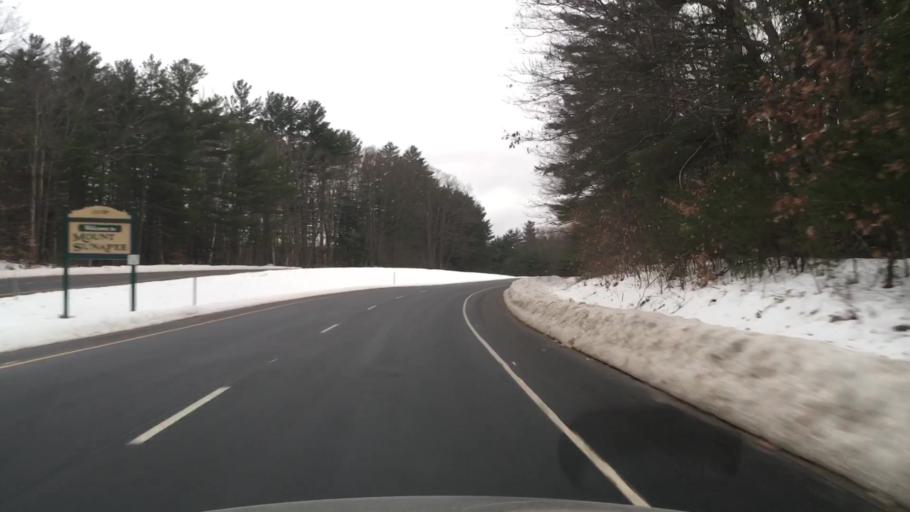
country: US
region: New Hampshire
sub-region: Merrimack County
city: Newbury
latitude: 43.3389
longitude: -72.0718
